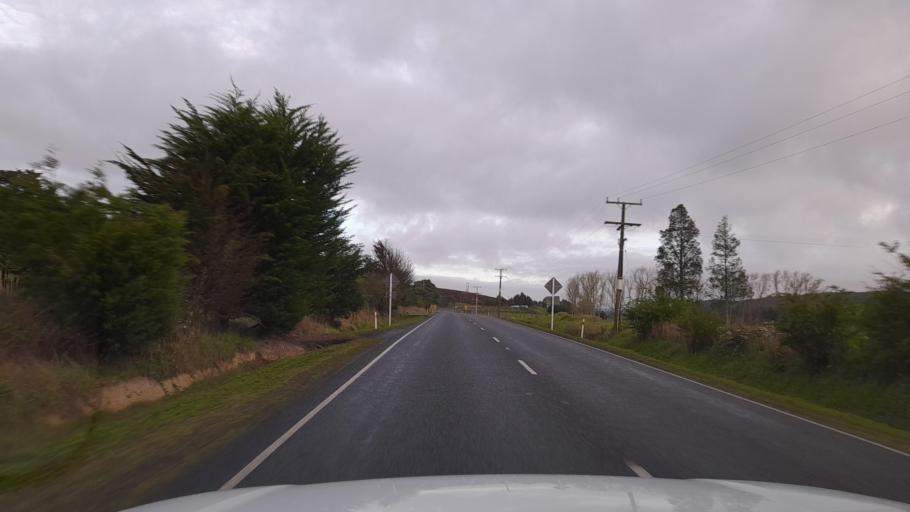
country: NZ
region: Northland
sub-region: Whangarei
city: Maungatapere
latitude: -35.7117
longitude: 174.0290
